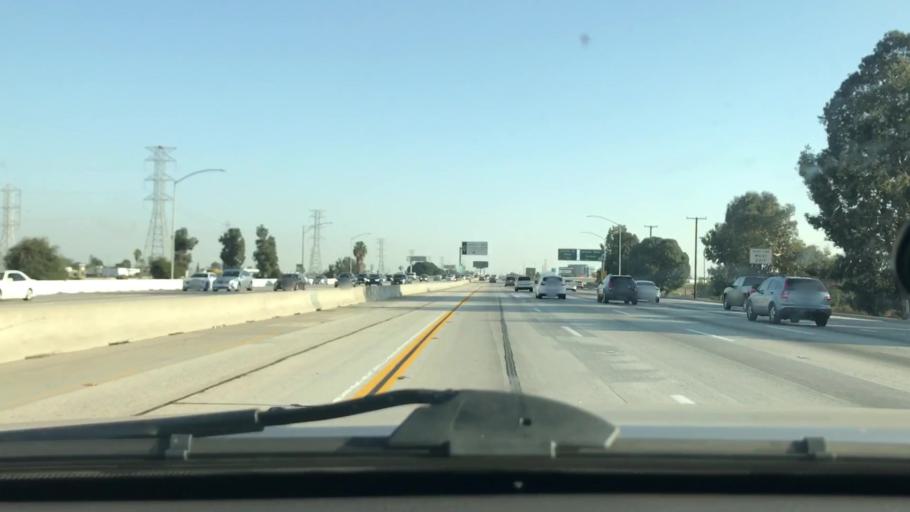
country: US
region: California
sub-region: Los Angeles County
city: Carson
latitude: 33.8426
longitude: -118.2667
